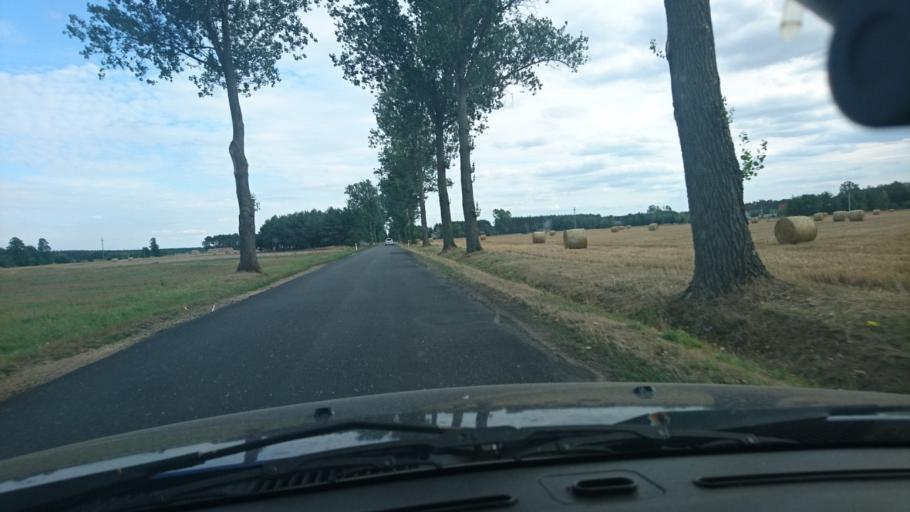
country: PL
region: Greater Poland Voivodeship
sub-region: Powiat ostrzeszowski
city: Kobyla Gora
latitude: 51.4543
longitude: 17.8170
